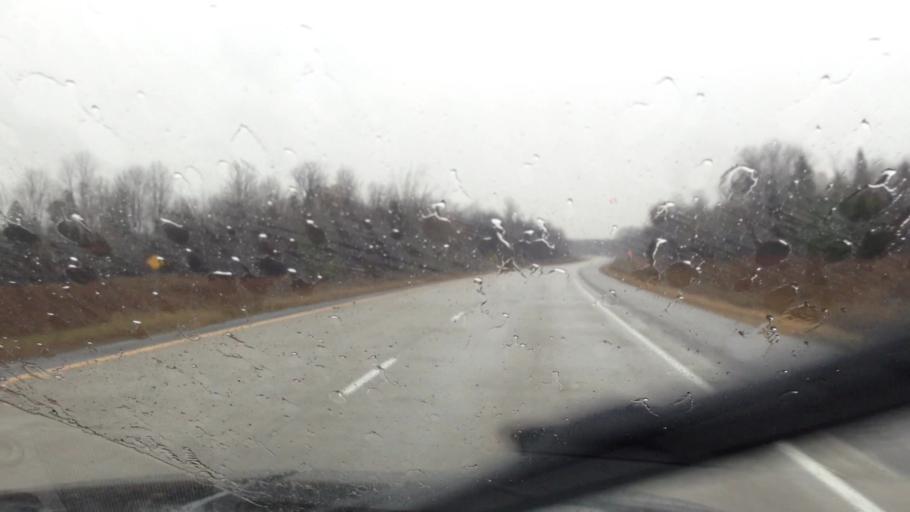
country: CA
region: Ontario
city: Hawkesbury
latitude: 45.4475
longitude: -74.7186
